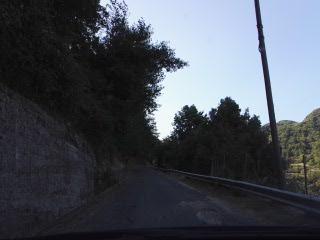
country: IT
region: Calabria
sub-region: Provincia di Vibo-Valentia
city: Nardodipace
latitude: 38.4439
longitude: 16.3405
